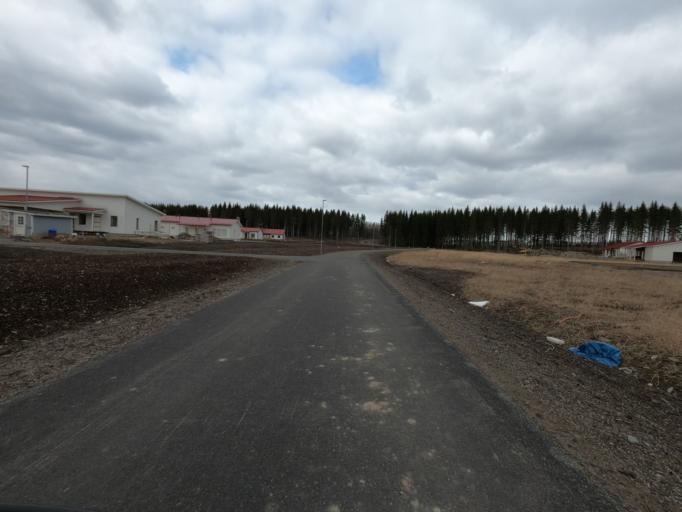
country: FI
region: North Karelia
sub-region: Joensuu
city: Joensuu
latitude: 62.5586
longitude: 29.8240
